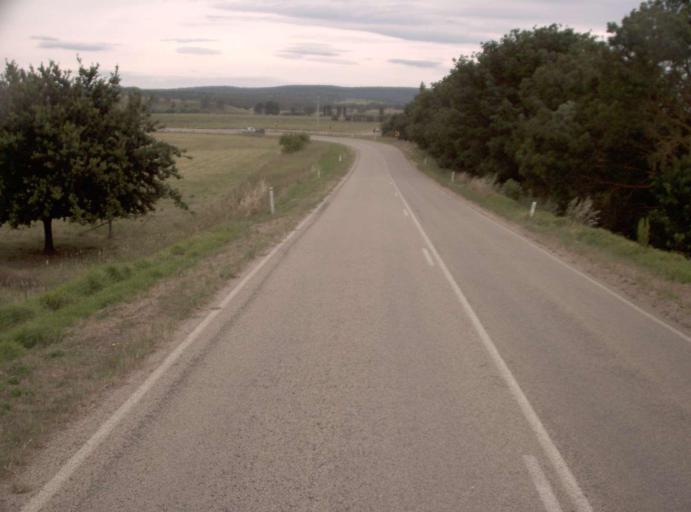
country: AU
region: Victoria
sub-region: East Gippsland
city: Bairnsdale
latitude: -37.8053
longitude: 147.4767
